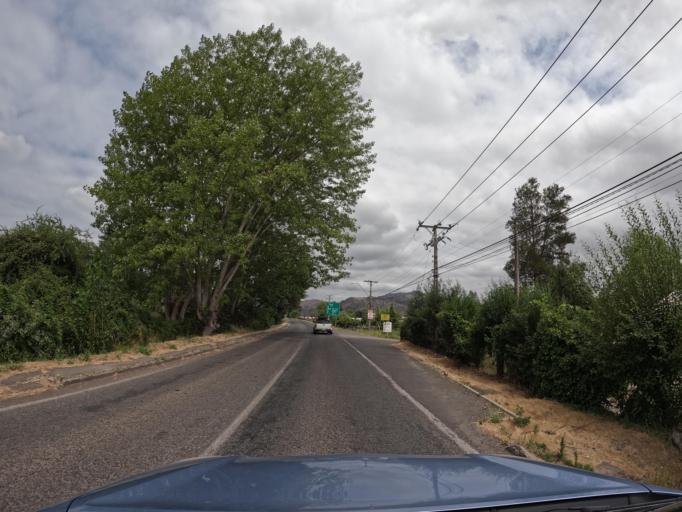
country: CL
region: Maule
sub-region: Provincia de Curico
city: Teno
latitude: -34.8597
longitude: -71.1857
